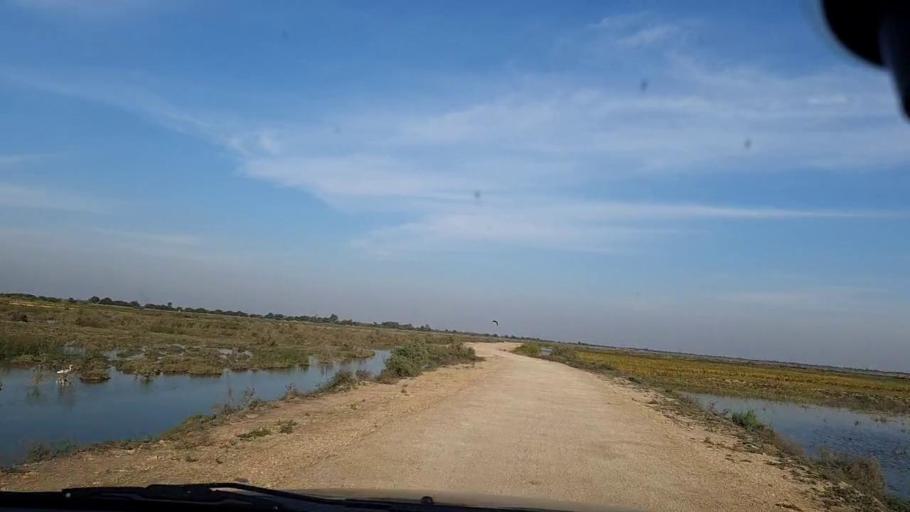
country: PK
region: Sindh
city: Mirpur Batoro
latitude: 24.6573
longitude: 68.3038
